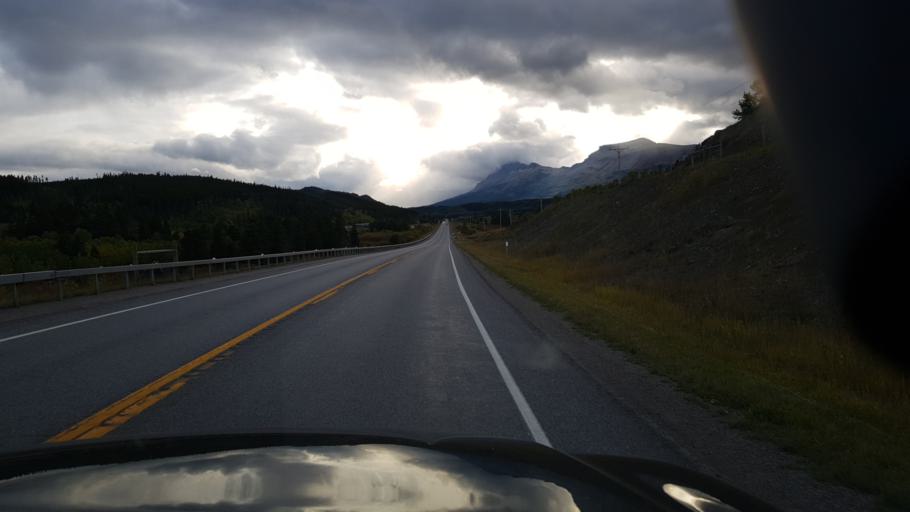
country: US
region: Montana
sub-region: Glacier County
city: South Browning
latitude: 48.4204
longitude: -113.2147
